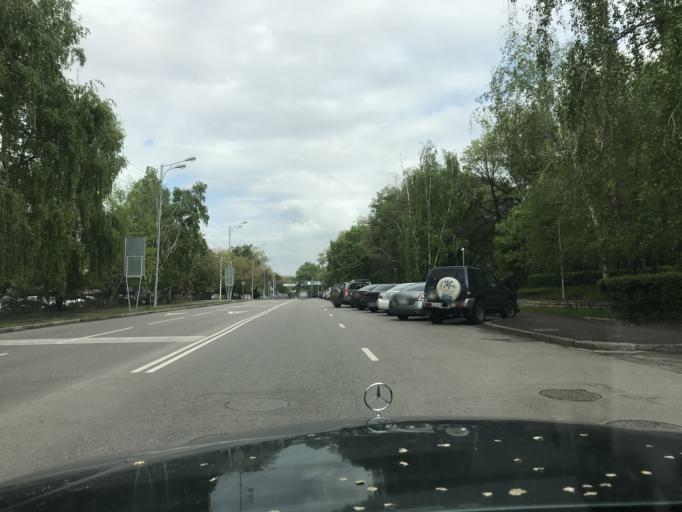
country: KZ
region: Almaty Qalasy
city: Almaty
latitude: 43.2056
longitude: 76.8749
